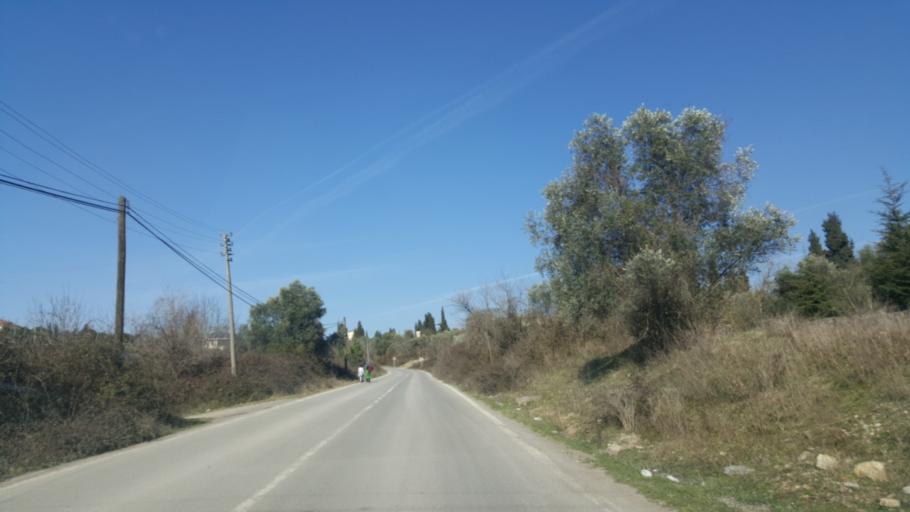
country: TR
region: Kocaeli
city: Tavsancil
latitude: 40.7783
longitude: 29.5749
